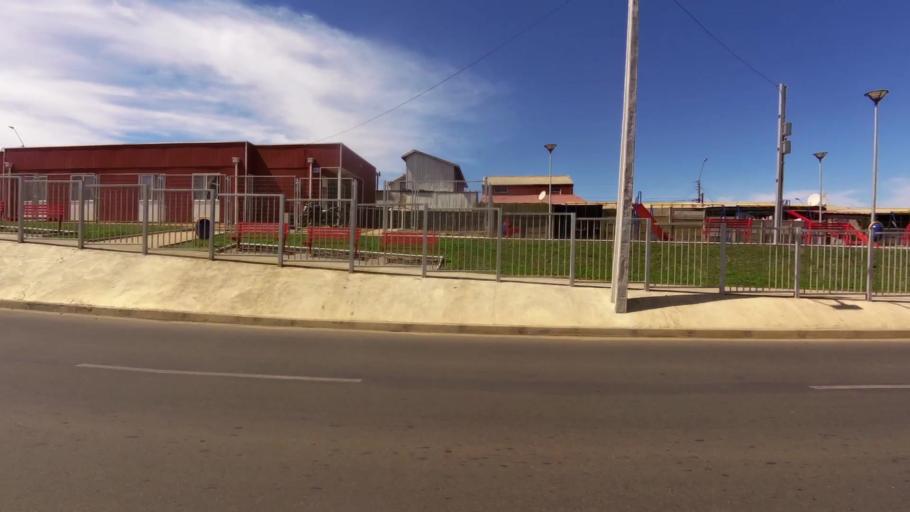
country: CL
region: Biobio
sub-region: Provincia de Concepcion
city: Talcahuano
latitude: -36.7121
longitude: -73.1338
